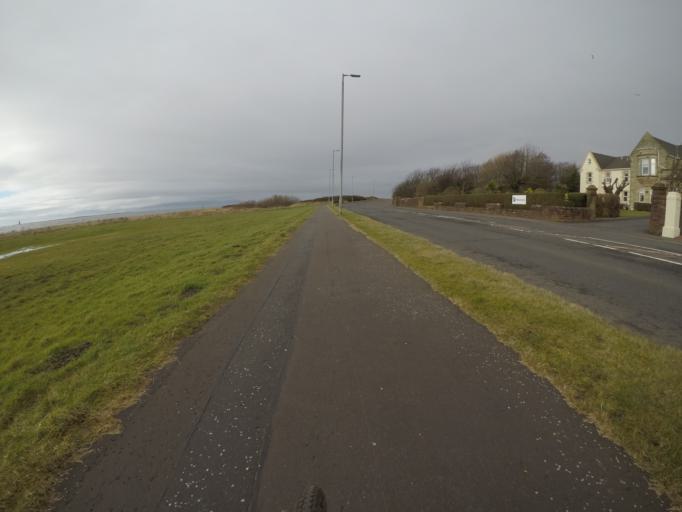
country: GB
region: Scotland
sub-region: North Ayrshire
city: Ardrossan
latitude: 55.6521
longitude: -4.8201
